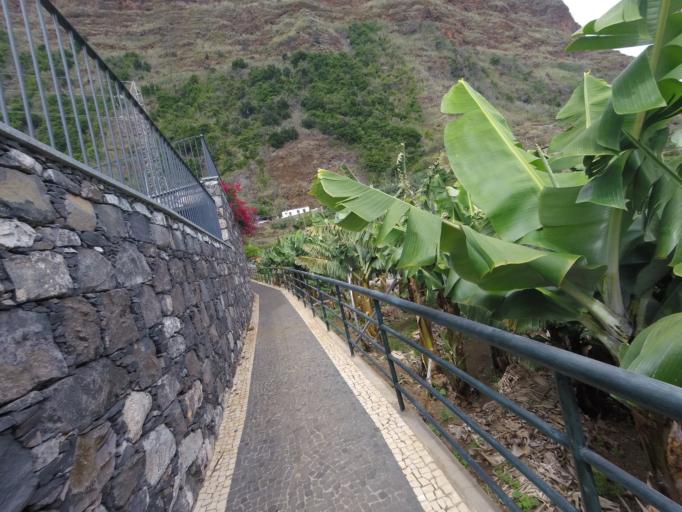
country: PT
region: Madeira
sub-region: Calheta
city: Estreito da Calheta
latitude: 32.7373
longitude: -17.2104
